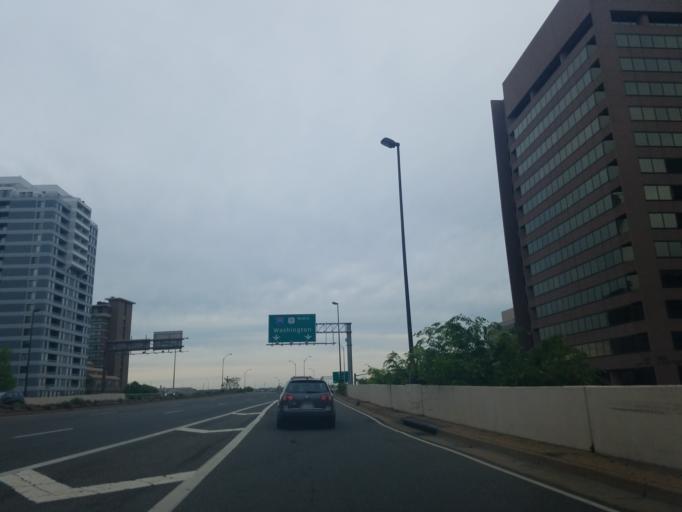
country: US
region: Washington, D.C.
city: Washington, D.C.
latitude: 38.8620
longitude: -77.0515
